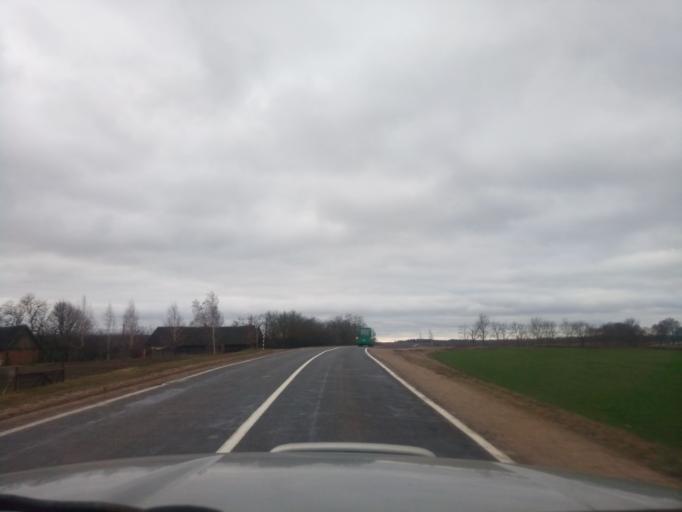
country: BY
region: Minsk
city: Kapyl'
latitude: 53.1731
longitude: 27.1611
